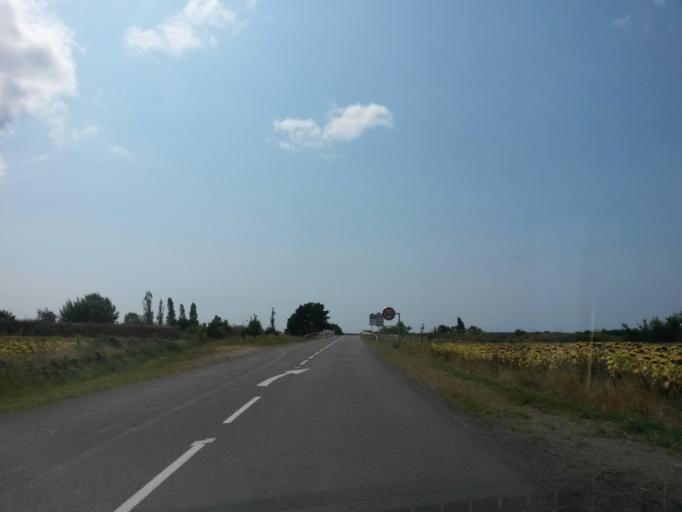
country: FR
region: Pays de la Loire
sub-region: Departement de la Vendee
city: Saint-Hilaire-de-Talmont
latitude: 46.4593
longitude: -1.6181
